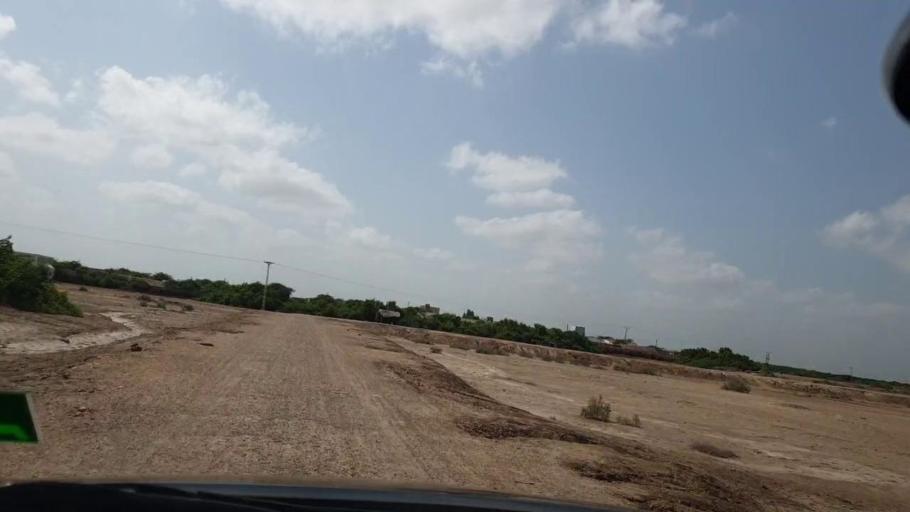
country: PK
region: Sindh
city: Kadhan
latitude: 24.5881
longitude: 69.1593
